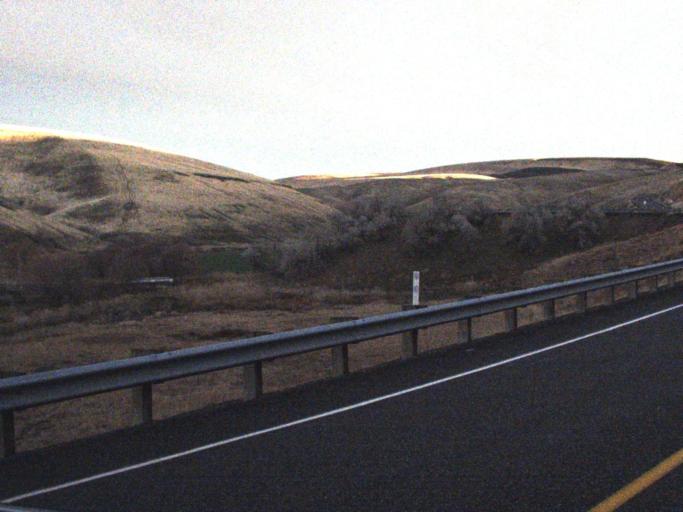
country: US
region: Washington
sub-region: Garfield County
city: Pomeroy
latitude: 46.5987
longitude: -117.7849
